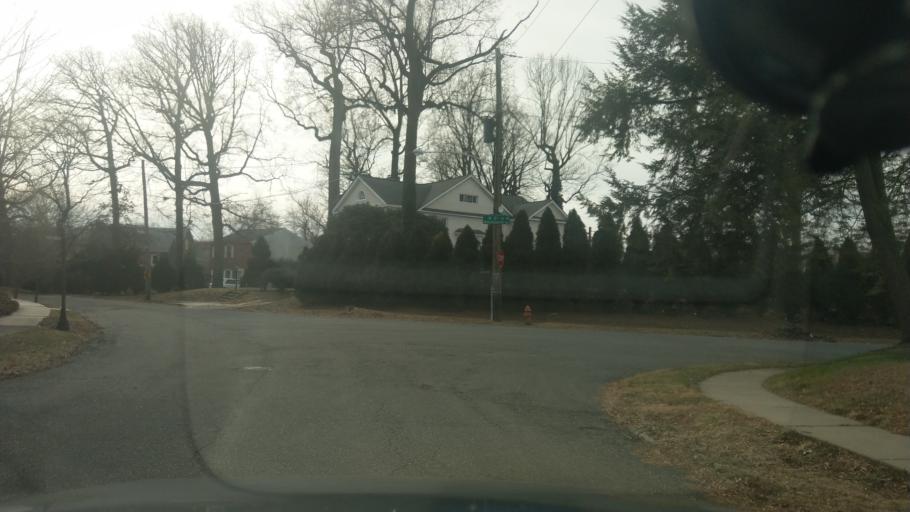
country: US
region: Pennsylvania
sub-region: Montgomery County
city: Jenkintown
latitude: 40.0475
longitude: -75.1340
